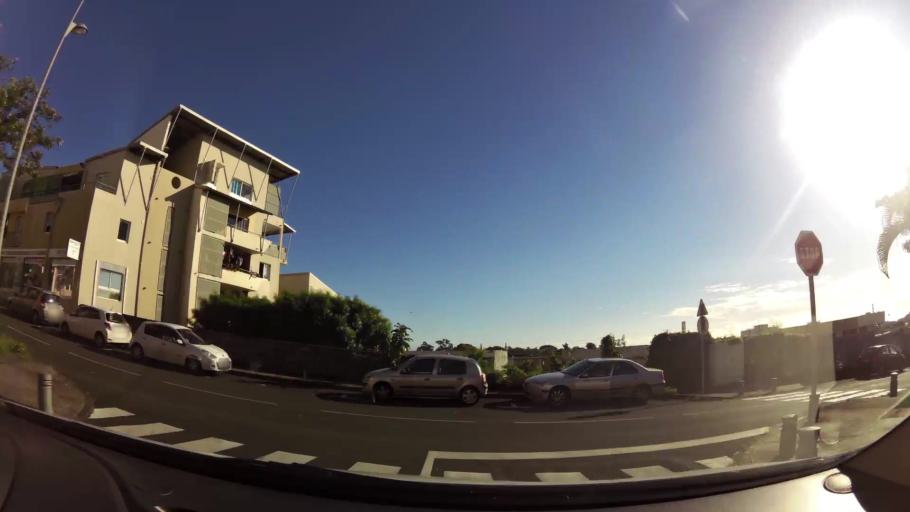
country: RE
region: Reunion
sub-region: Reunion
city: Saint-Denis
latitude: -20.8927
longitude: 55.4510
